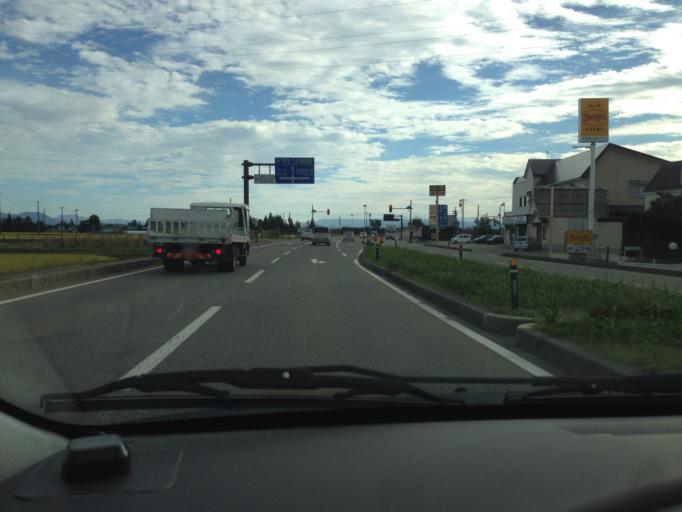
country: JP
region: Fukushima
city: Inawashiro
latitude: 37.5498
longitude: 140.1132
